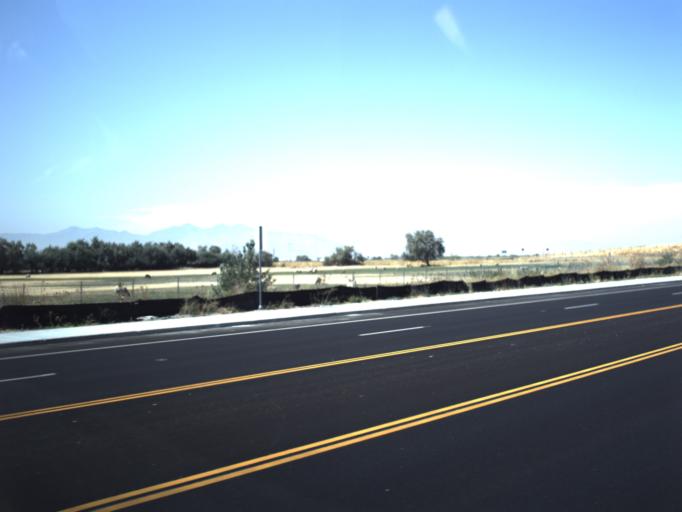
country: US
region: Utah
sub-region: Davis County
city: West Bountiful
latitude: 40.8841
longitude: -111.9323
